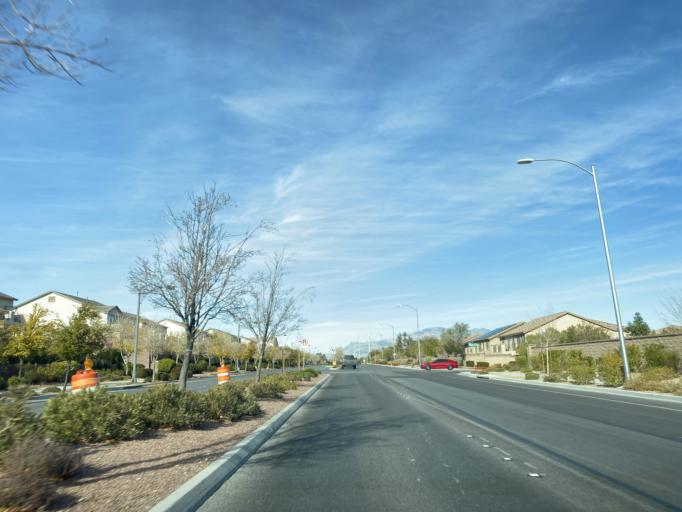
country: US
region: Nevada
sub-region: Clark County
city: Summerlin South
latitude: 36.2952
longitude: -115.3149
